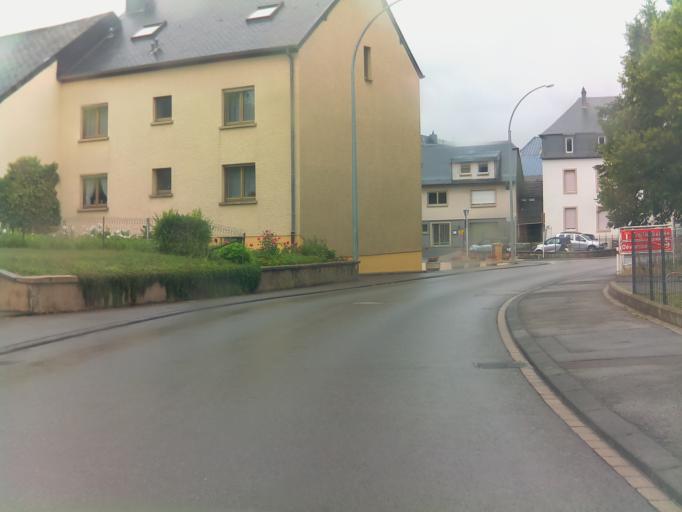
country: LU
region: Luxembourg
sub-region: Canton de Capellen
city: Clemency
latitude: 49.5934
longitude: 5.8779
